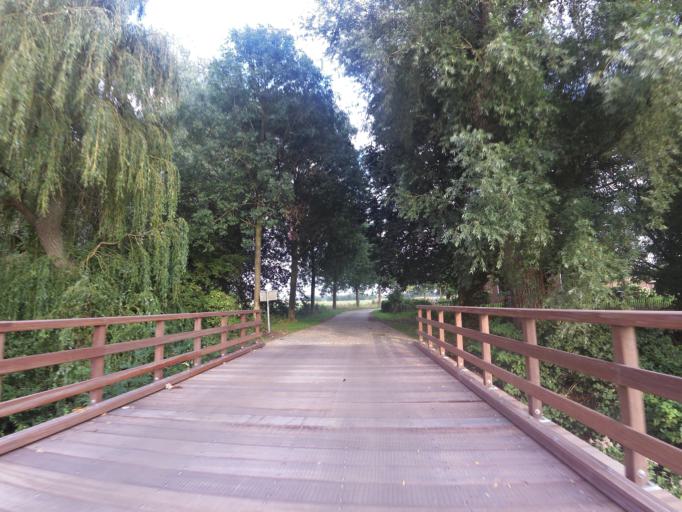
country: NL
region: Gelderland
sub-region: Gemeente Doetinchem
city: Doetinchem
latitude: 51.9374
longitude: 6.2983
